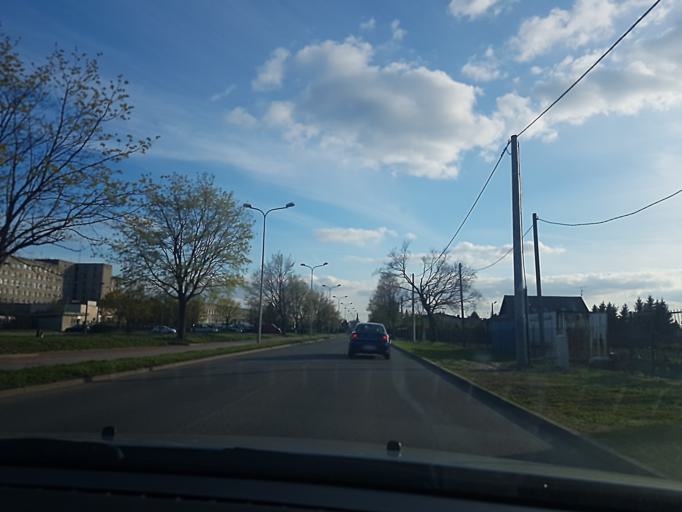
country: PL
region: Lodz Voivodeship
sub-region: Powiat kutnowski
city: Kutno
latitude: 52.2411
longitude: 19.3728
